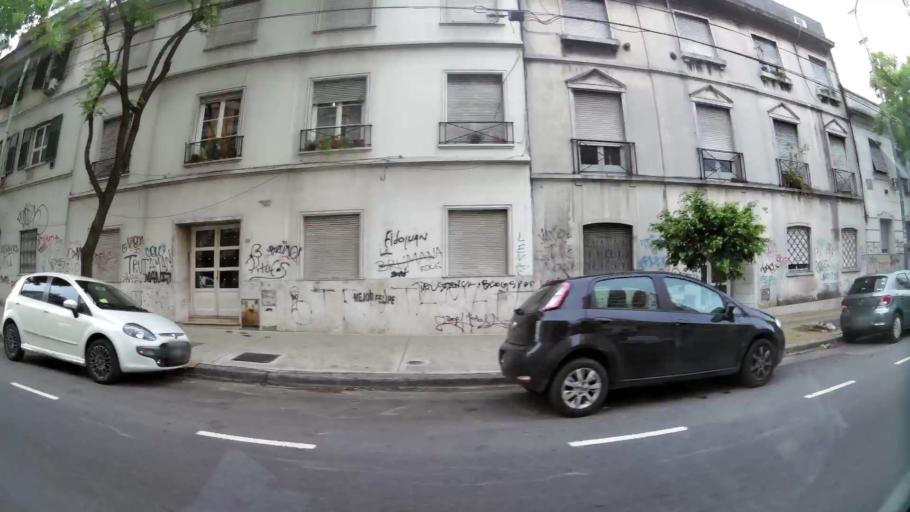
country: AR
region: Buenos Aires F.D.
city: Villa Santa Rita
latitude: -34.6339
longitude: -58.4617
